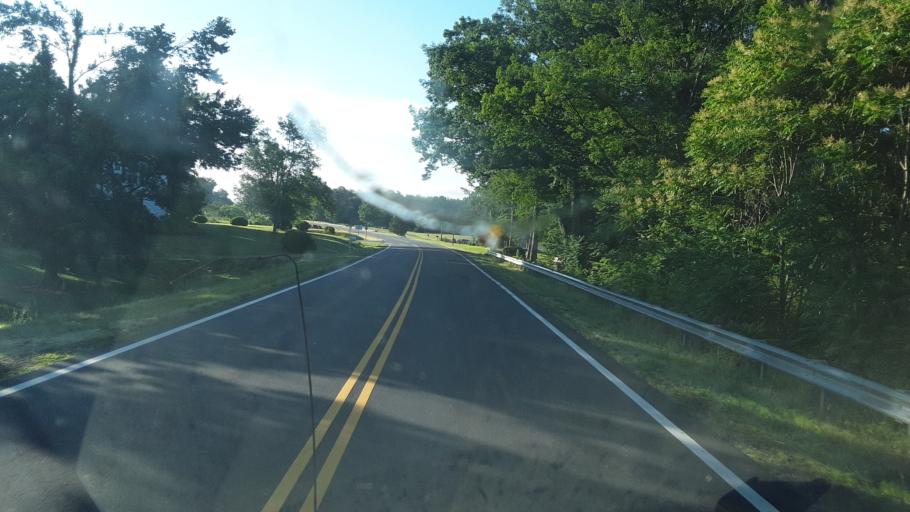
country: US
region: Virginia
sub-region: Pittsylvania County
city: Chatham
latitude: 36.8350
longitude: -79.4406
